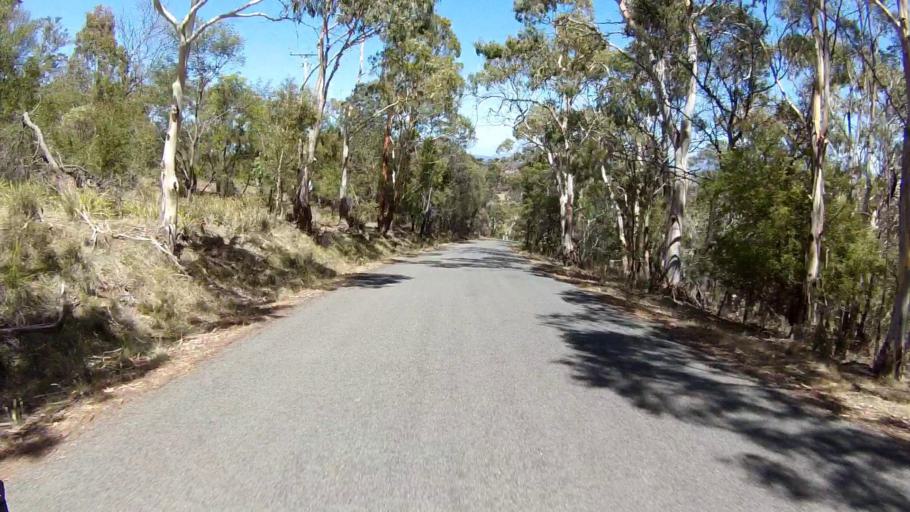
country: AU
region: Tasmania
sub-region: Clarence
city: Cambridge
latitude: -42.8497
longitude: 147.4302
